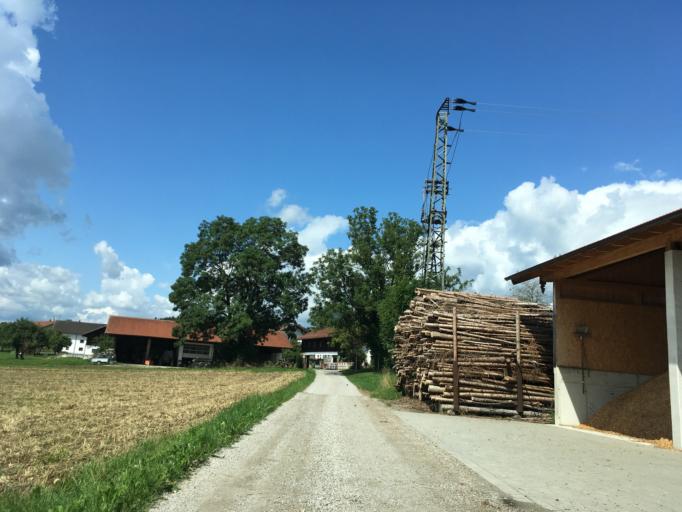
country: DE
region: Bavaria
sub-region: Upper Bavaria
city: Pittenhart
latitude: 47.9683
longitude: 12.3774
